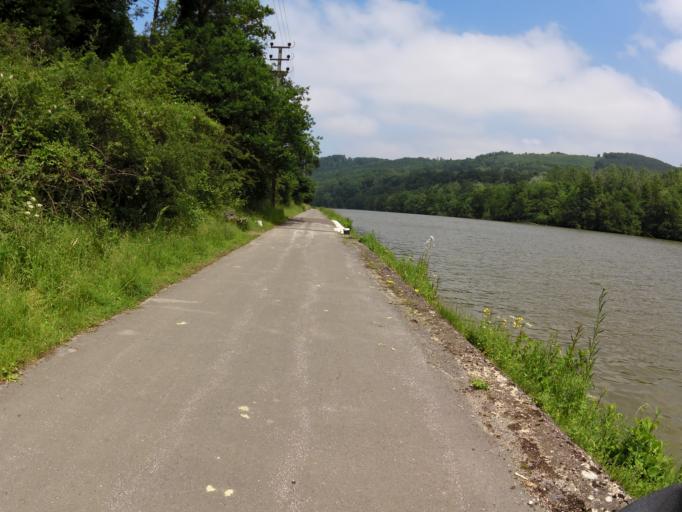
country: BE
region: Wallonia
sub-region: Province de Namur
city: Hastiere-Lavaux
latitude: 50.1831
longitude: 4.8234
